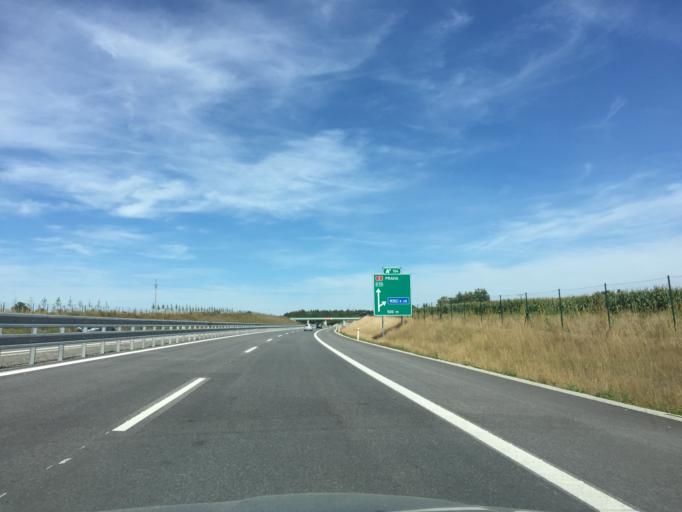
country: CZ
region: Jihocesky
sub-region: Okres Tabor
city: Veseli nad Luznici
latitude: 49.1921
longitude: 14.6887
